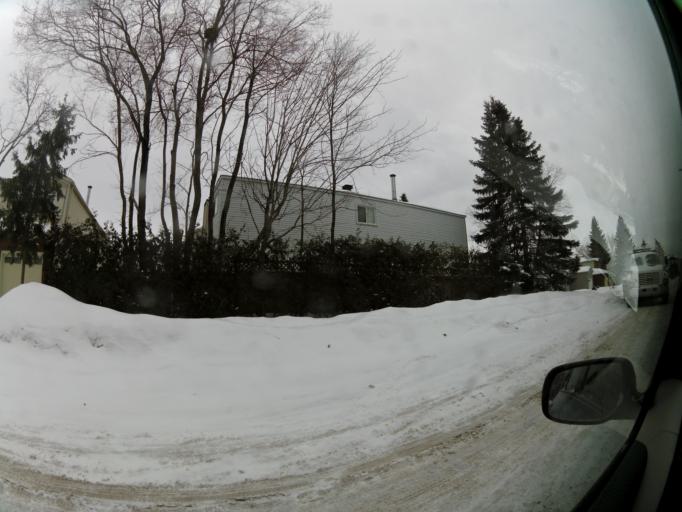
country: CA
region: Ontario
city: Ottawa
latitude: 45.3722
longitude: -75.6216
